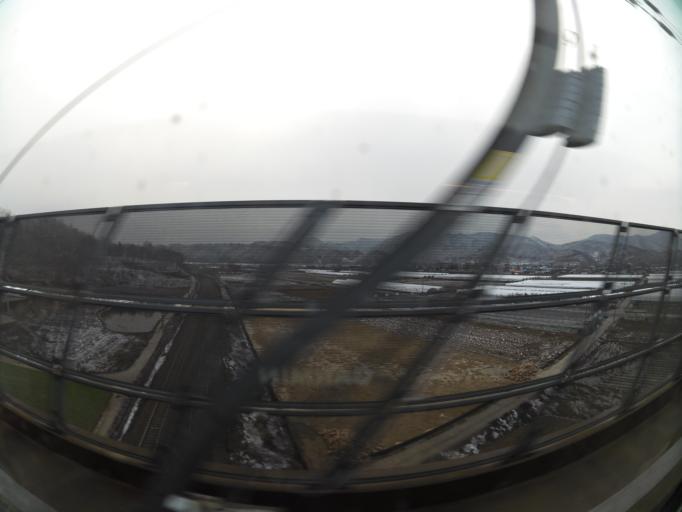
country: KR
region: Chungcheongbuk-do
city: Yong-dong
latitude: 36.2183
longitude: 127.7205
